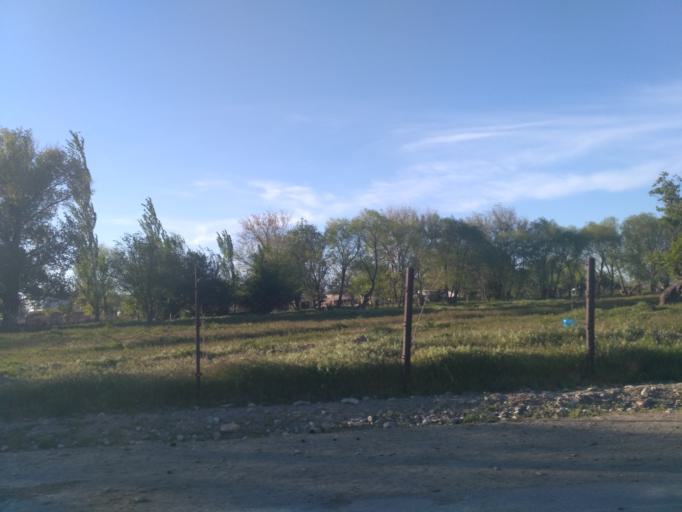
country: KZ
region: Ongtustik Qazaqstan
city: Ashchysay
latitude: 43.6930
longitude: 68.9925
